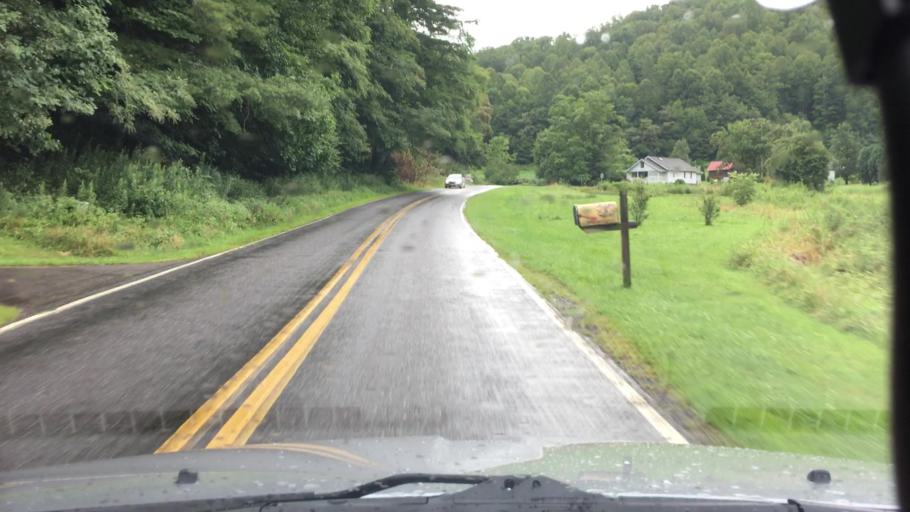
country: US
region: North Carolina
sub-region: Madison County
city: Mars Hill
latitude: 35.9129
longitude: -82.4768
